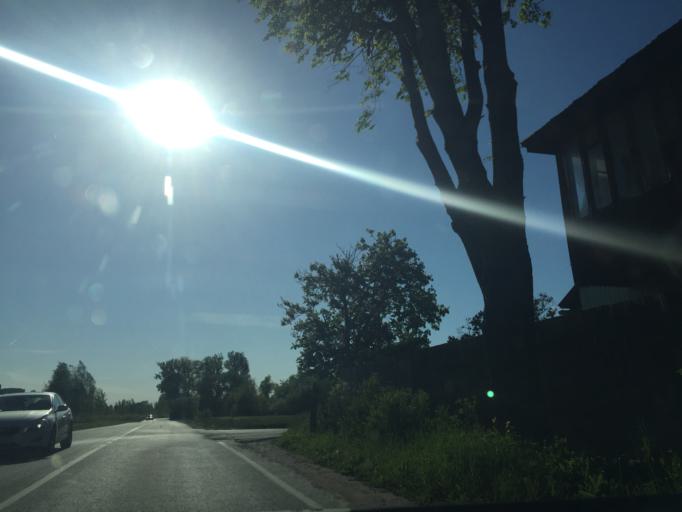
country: LT
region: Panevezys
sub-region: Panevezys City
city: Panevezys
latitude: 55.7460
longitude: 24.3387
